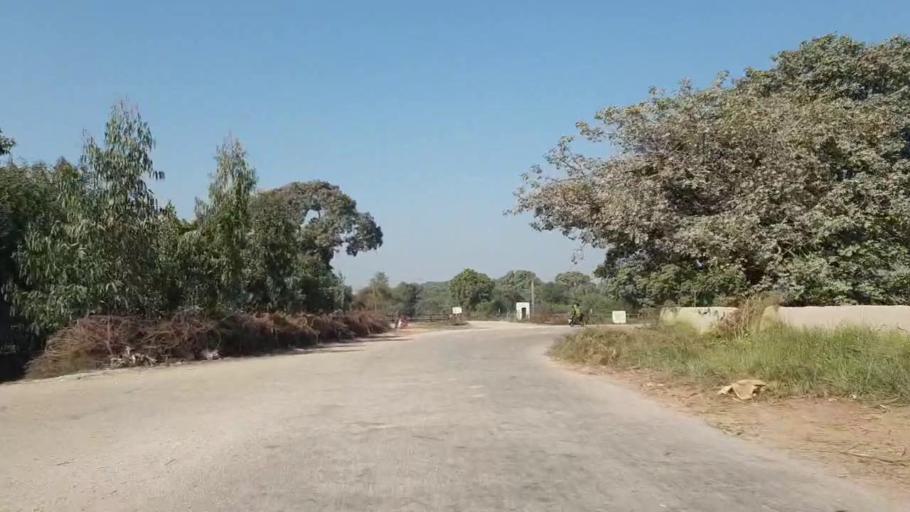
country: PK
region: Sindh
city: Matiari
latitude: 25.6203
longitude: 68.5916
